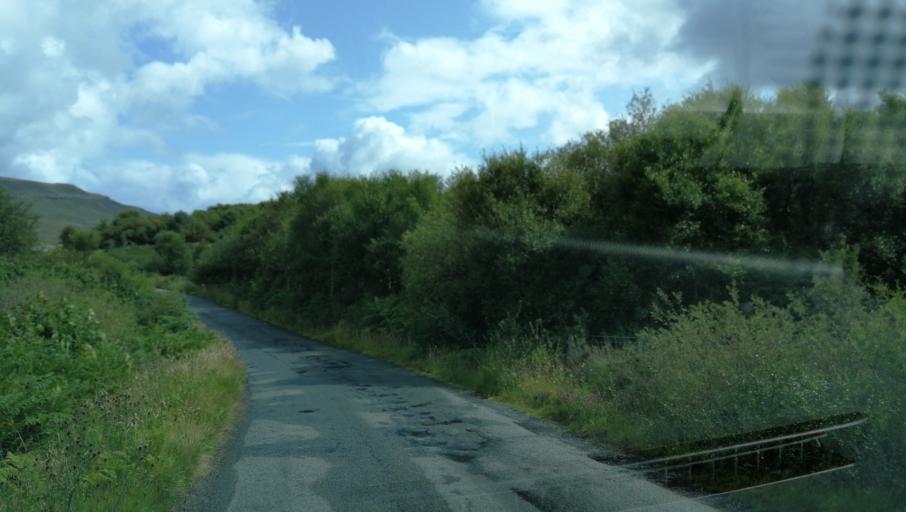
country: GB
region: Scotland
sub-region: Highland
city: Portree
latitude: 57.3832
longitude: -6.1822
